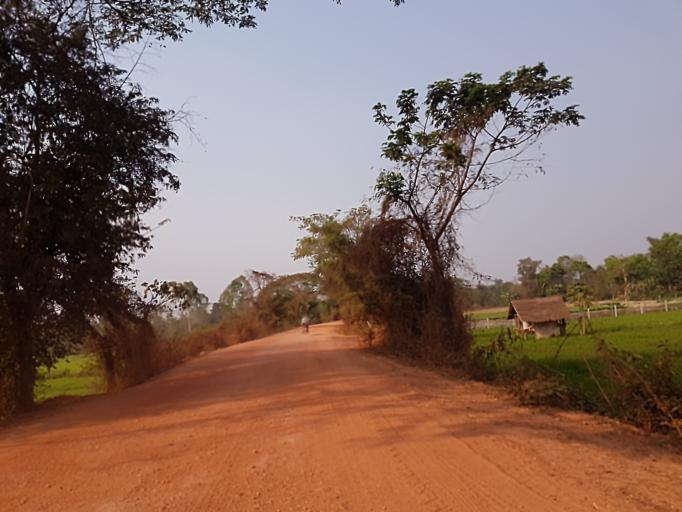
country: TH
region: Nong Khai
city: Phon Phisai
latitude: 18.0044
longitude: 102.9079
